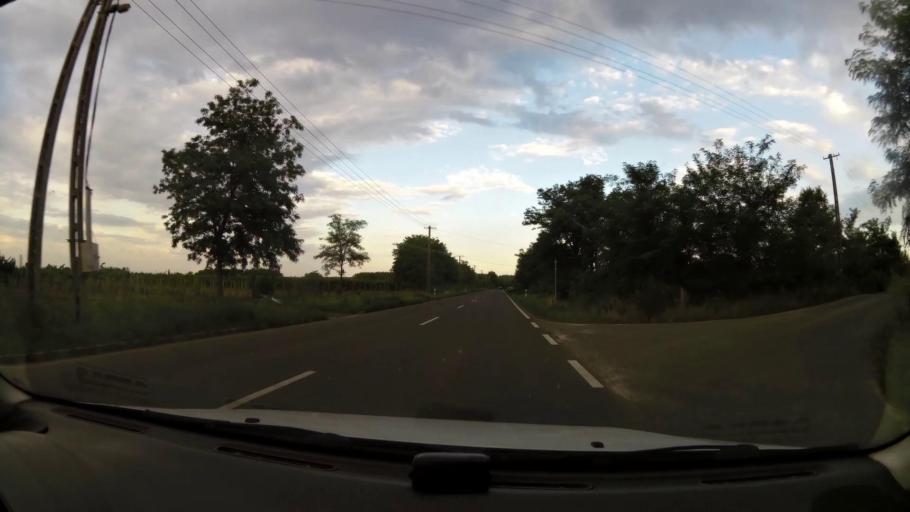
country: HU
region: Pest
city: Tapioszele
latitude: 47.3073
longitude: 19.8808
